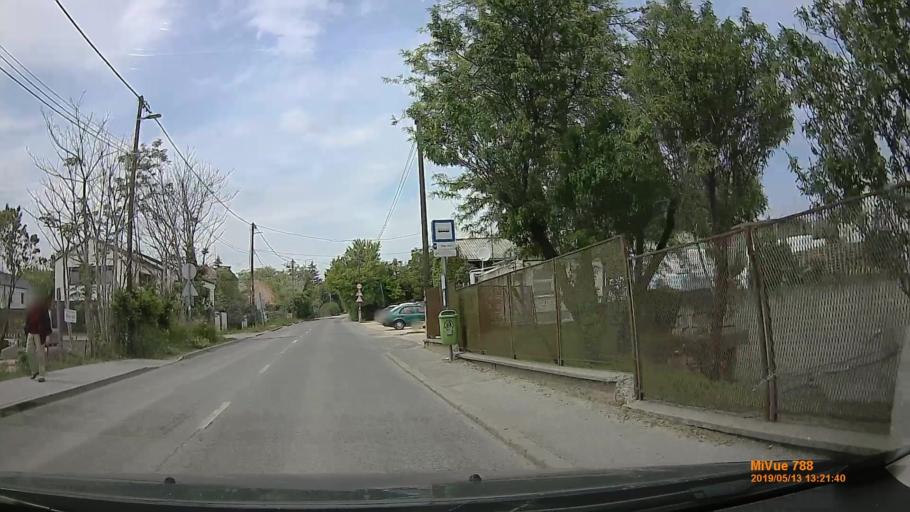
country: HU
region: Budapest
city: Budapest XXII. keruelet
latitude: 47.4120
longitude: 19.0052
